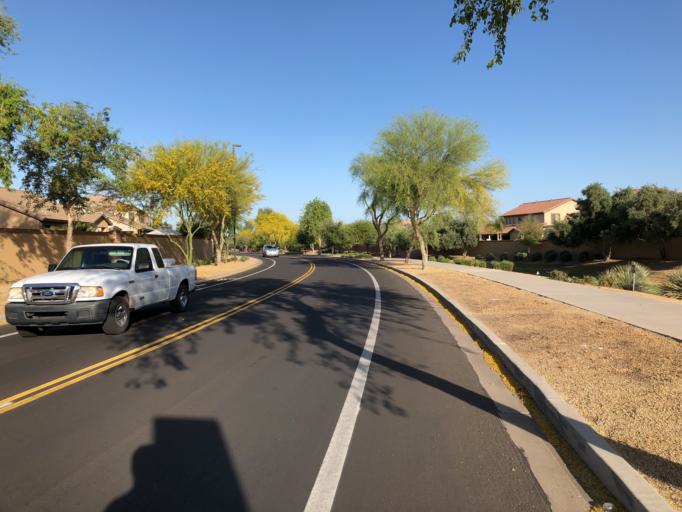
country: US
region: Arizona
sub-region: Maricopa County
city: Queen Creek
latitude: 33.2269
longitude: -111.7131
